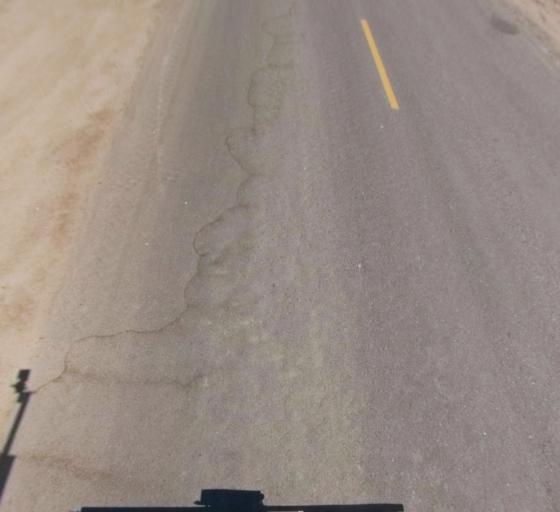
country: US
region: California
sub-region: Fresno County
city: Biola
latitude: 36.8731
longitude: -119.9471
